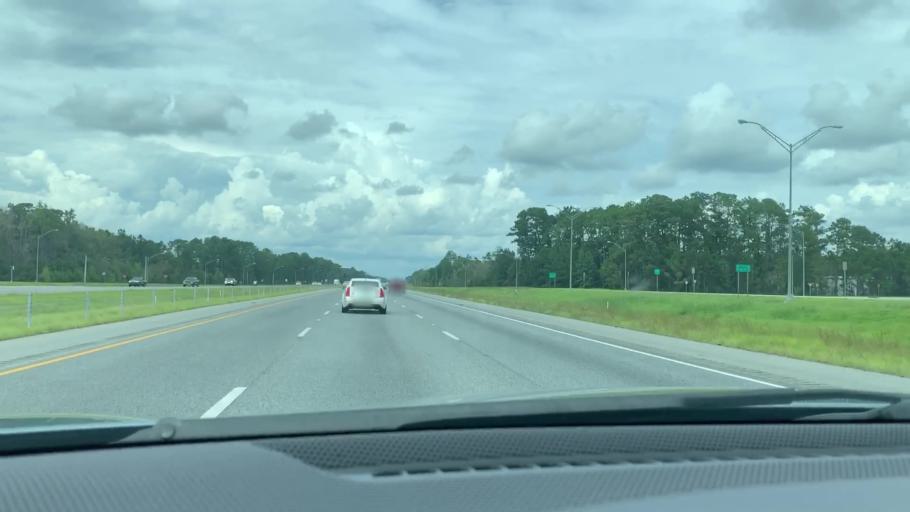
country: US
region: Georgia
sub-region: McIntosh County
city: Darien
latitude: 31.4778
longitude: -81.4471
